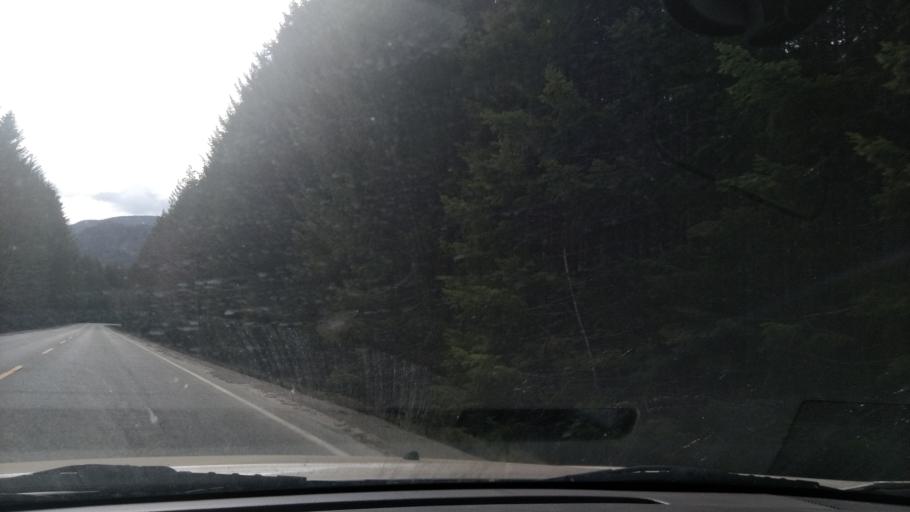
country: CA
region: British Columbia
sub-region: Regional District of Alberni-Clayoquot
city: Tofino
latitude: 49.8324
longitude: -125.9671
